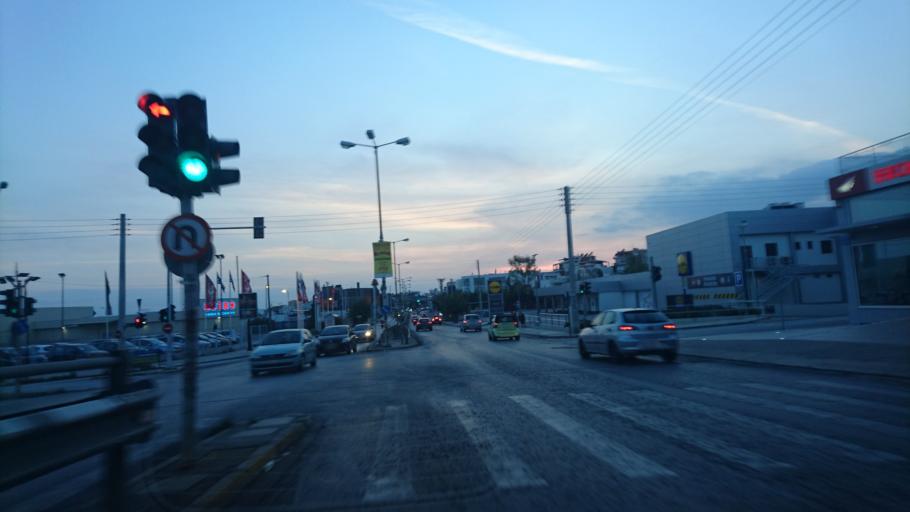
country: GR
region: Attica
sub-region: Nomarchia Athinas
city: Argyroupoli
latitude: 37.9089
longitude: 23.7380
